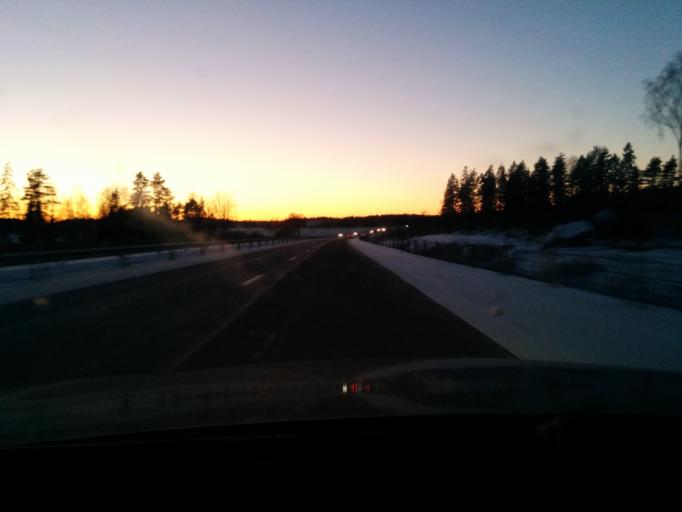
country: SE
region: Uppsala
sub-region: Enkopings Kommun
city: Hummelsta
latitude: 59.6229
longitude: 16.8151
